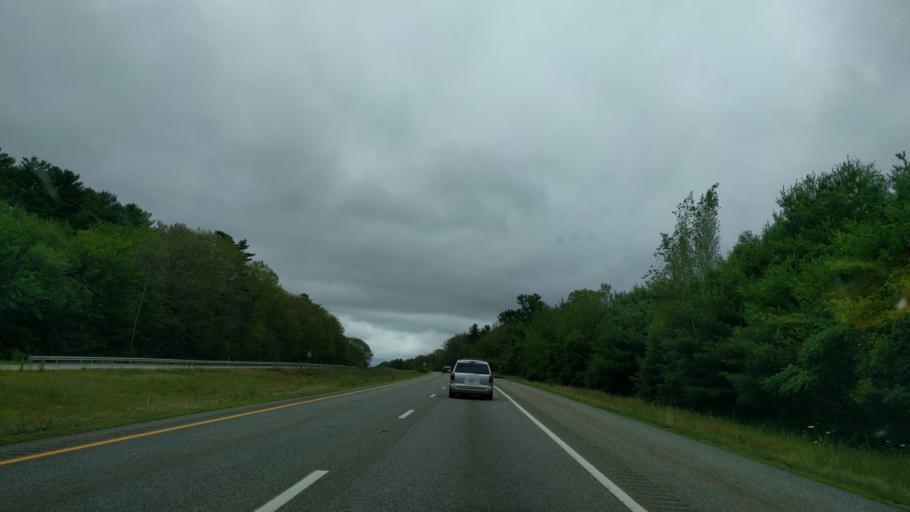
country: US
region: Massachusetts
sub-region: Worcester County
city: Millville
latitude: 42.0176
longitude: -71.5949
